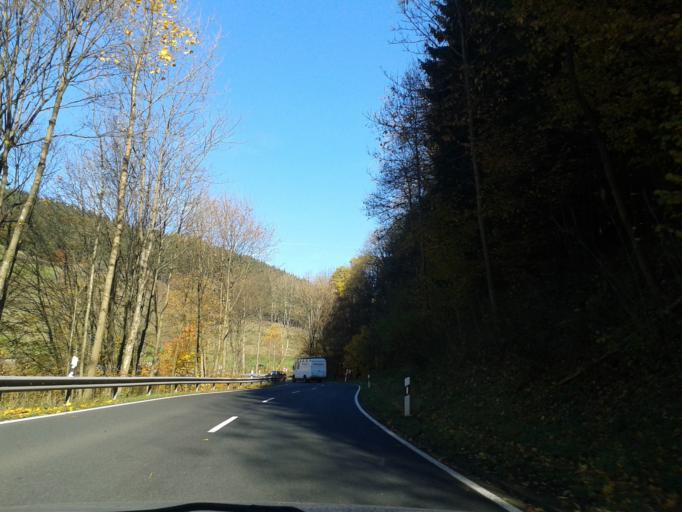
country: DE
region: North Rhine-Westphalia
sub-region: Regierungsbezirk Arnsberg
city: Bad Laasphe
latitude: 50.9638
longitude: 8.3483
